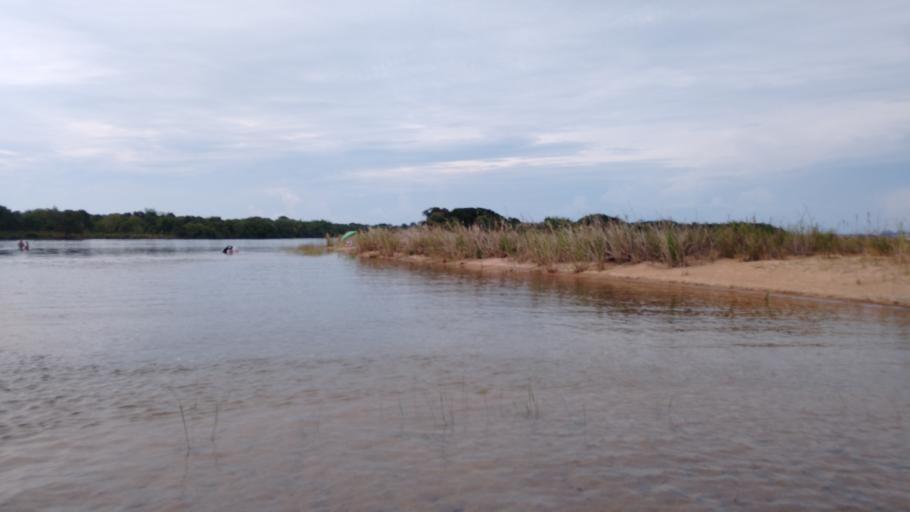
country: AR
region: Corrientes
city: Ituzaingo
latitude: -27.5656
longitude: -56.7036
